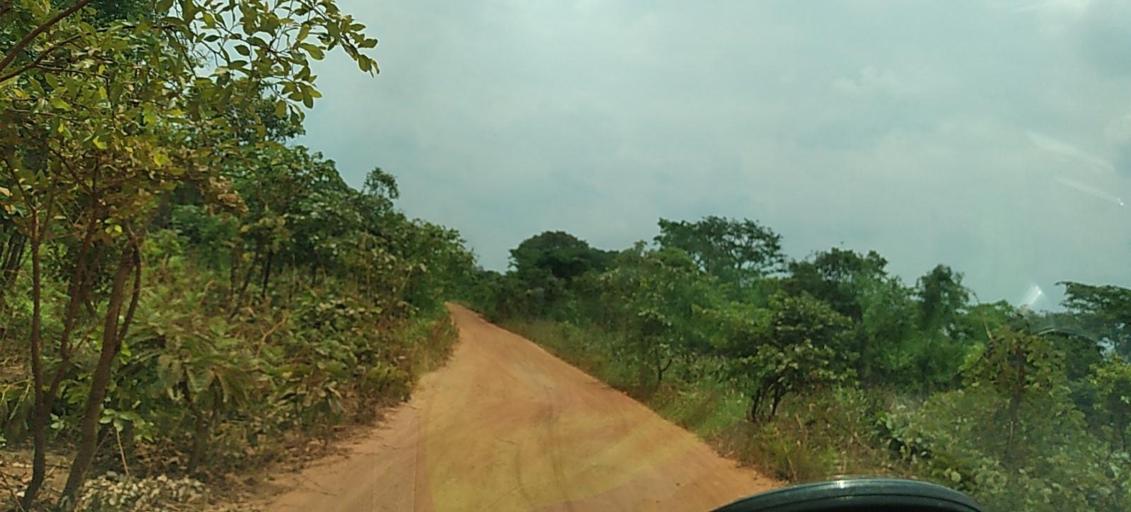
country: ZM
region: North-Western
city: Kansanshi
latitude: -12.0519
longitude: 26.3413
